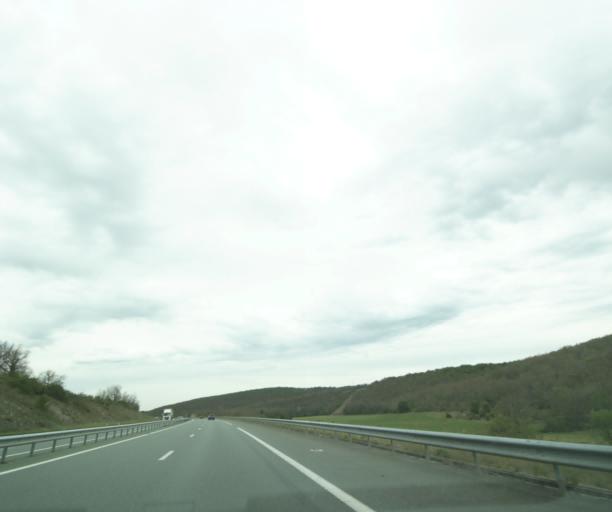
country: FR
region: Midi-Pyrenees
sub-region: Departement du Lot
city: Le Vigan
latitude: 44.7669
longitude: 1.5399
